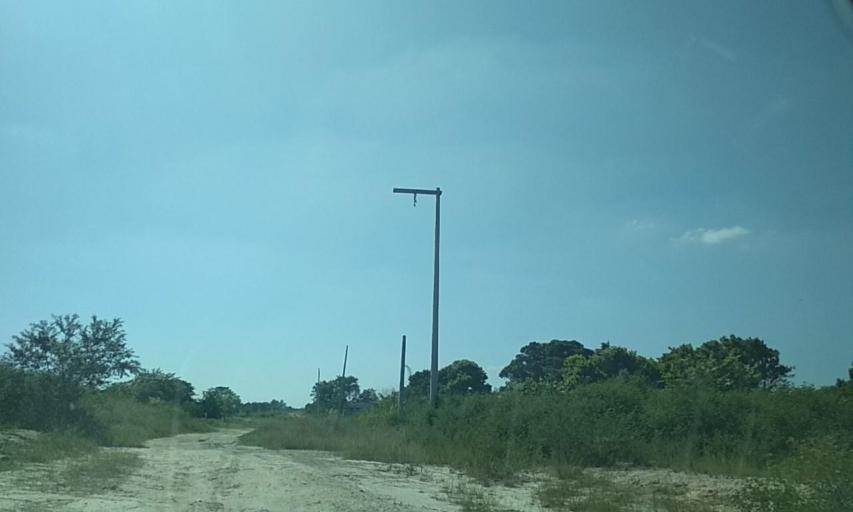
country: MX
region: Veracruz
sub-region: Martinez de la Torre
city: La Union Paso Largo
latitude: 20.1445
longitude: -97.0002
